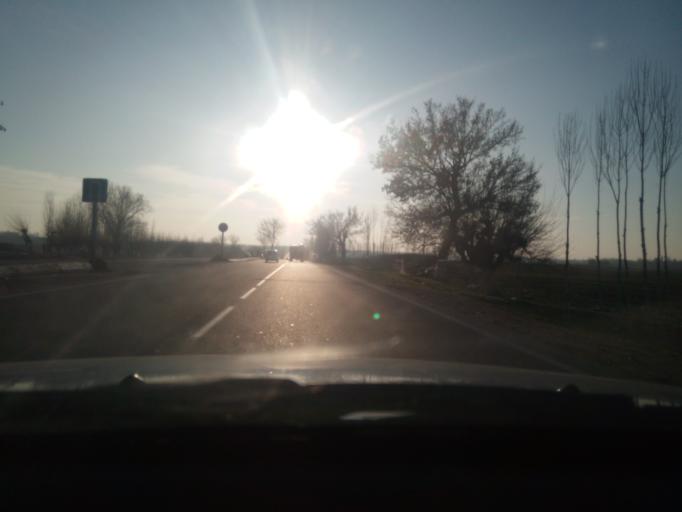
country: UZ
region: Toshkent
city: Yangiyul
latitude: 41.1367
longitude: 69.0171
